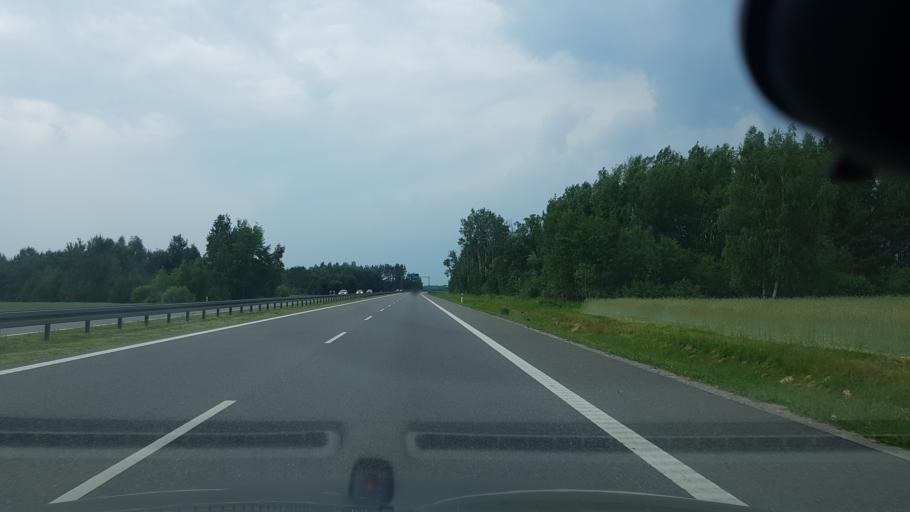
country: PL
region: Masovian Voivodeship
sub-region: Powiat legionowski
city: Serock
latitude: 52.4985
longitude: 21.0473
